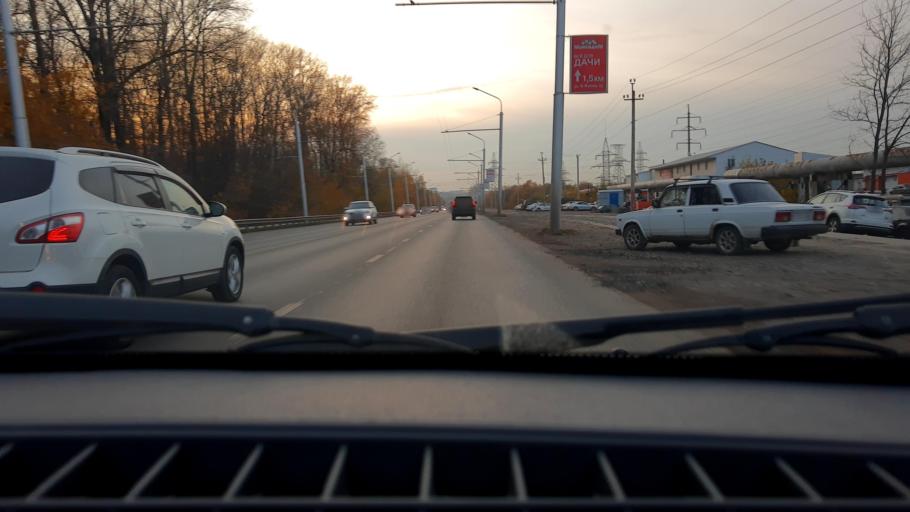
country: RU
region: Bashkortostan
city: Ufa
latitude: 54.7902
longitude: 56.0997
